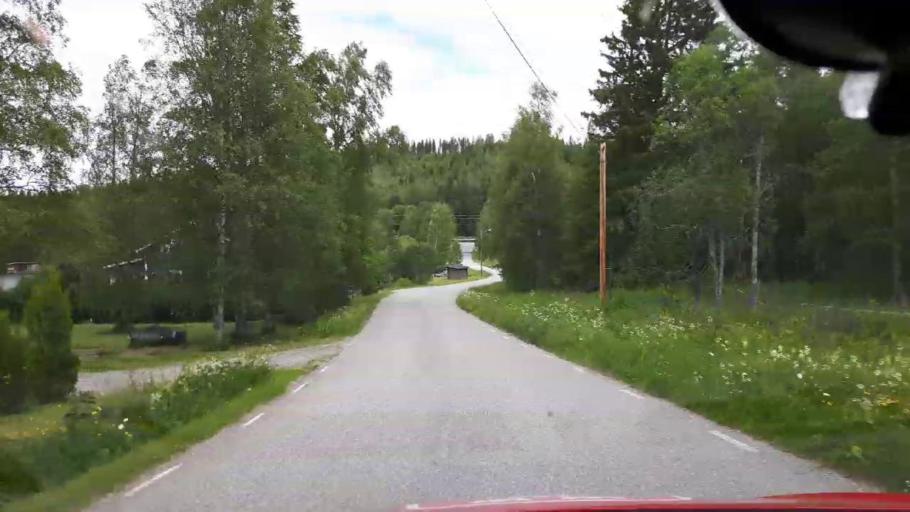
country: SE
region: Jaemtland
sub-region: Braecke Kommun
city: Braecke
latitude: 62.8860
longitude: 15.2729
